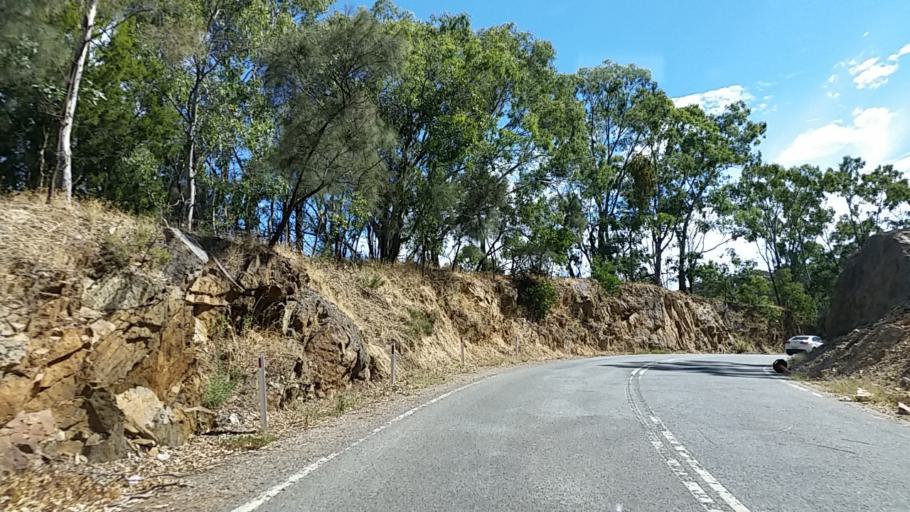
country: AU
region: South Australia
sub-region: Campbelltown
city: Athelstone
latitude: -34.8579
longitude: 138.7898
